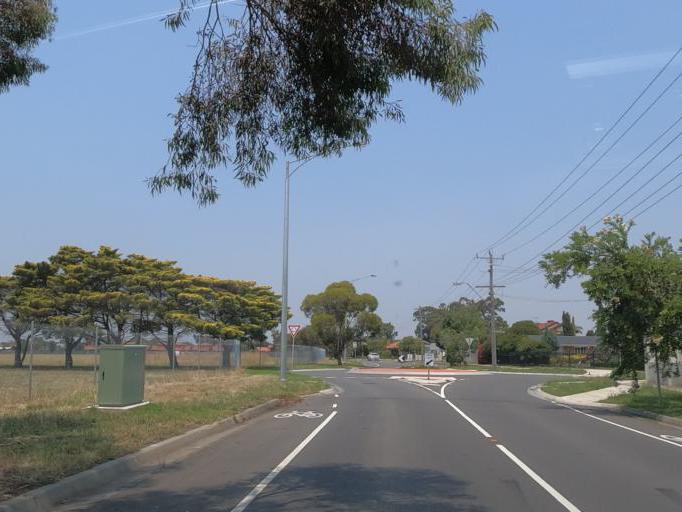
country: AU
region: Victoria
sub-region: Hume
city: Attwood
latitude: -37.6487
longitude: 144.8896
